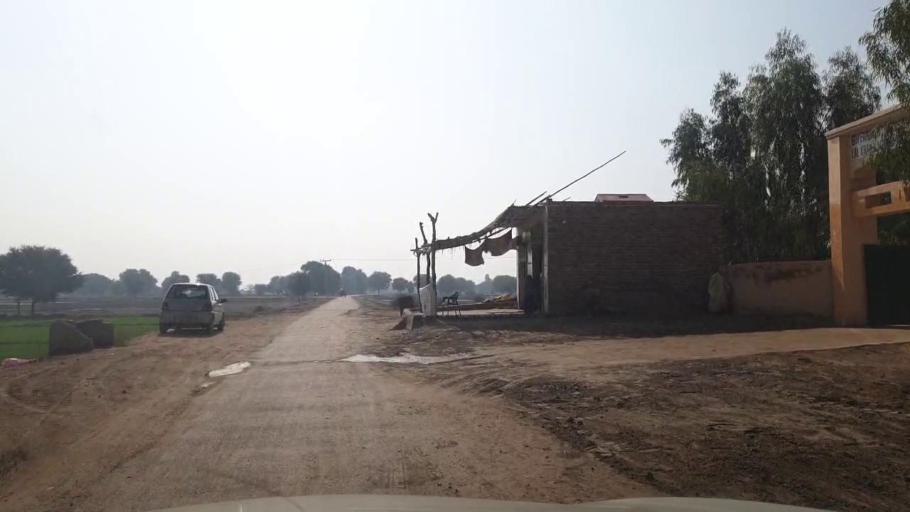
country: PK
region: Sindh
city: Bhan
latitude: 26.5068
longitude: 67.7897
